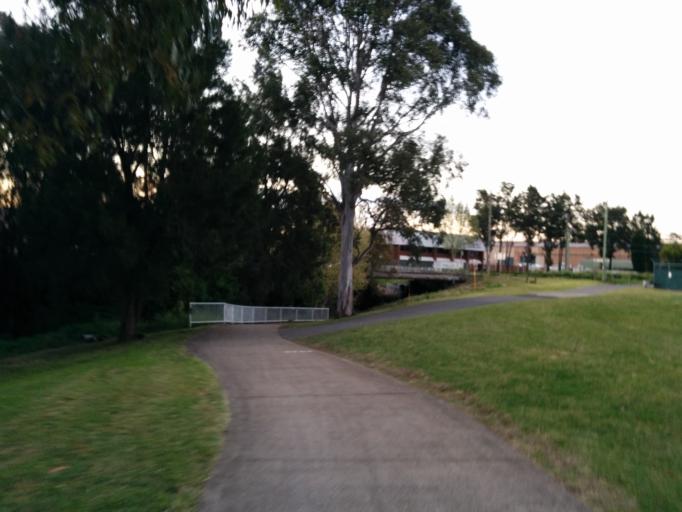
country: AU
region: New South Wales
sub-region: Fairfield
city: Fairfield Heights
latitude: -33.8508
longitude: 150.9454
